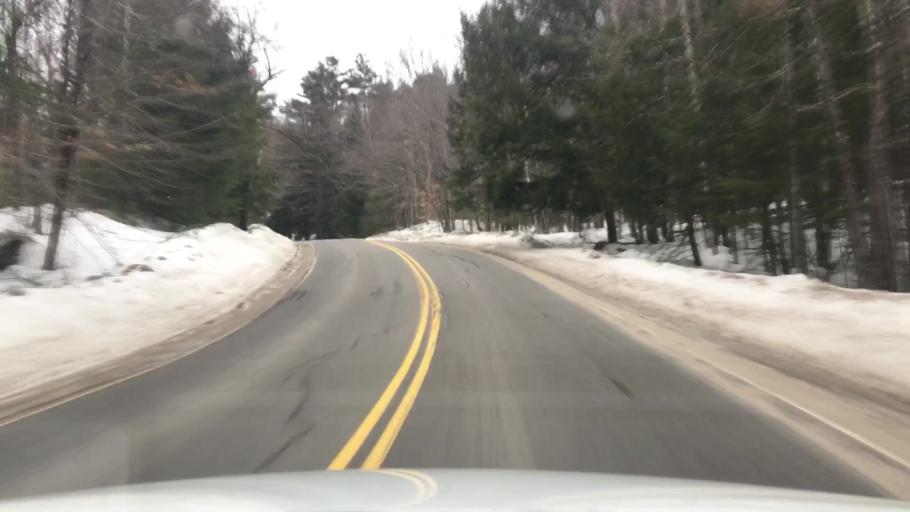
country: US
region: Maine
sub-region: Oxford County
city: Hiram
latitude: 43.8962
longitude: -70.7924
